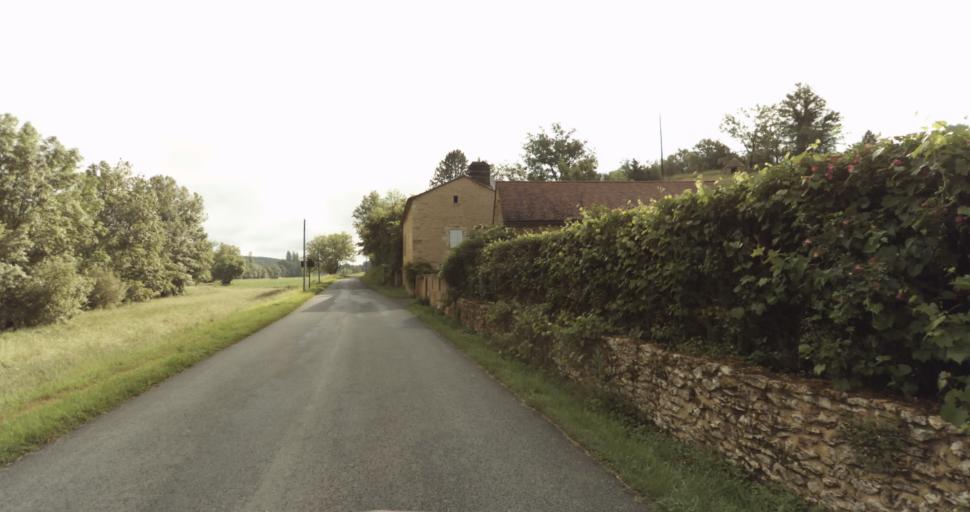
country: FR
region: Aquitaine
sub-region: Departement de la Dordogne
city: Lalinde
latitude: 44.9264
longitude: 0.7568
